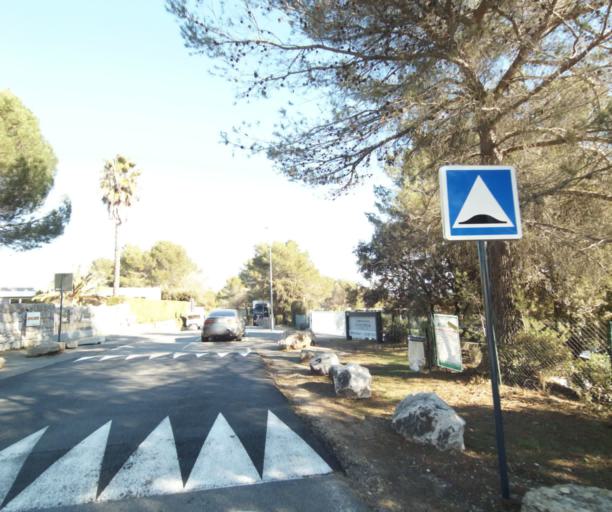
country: FR
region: Provence-Alpes-Cote d'Azur
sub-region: Departement des Alpes-Maritimes
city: Biot
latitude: 43.6074
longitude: 7.0702
